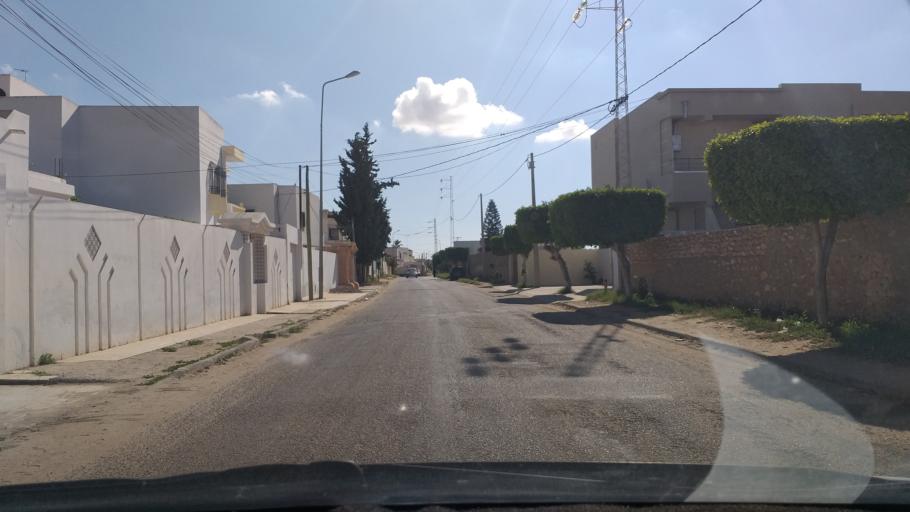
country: TN
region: Safaqis
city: Al Qarmadah
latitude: 34.8012
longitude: 10.7729
